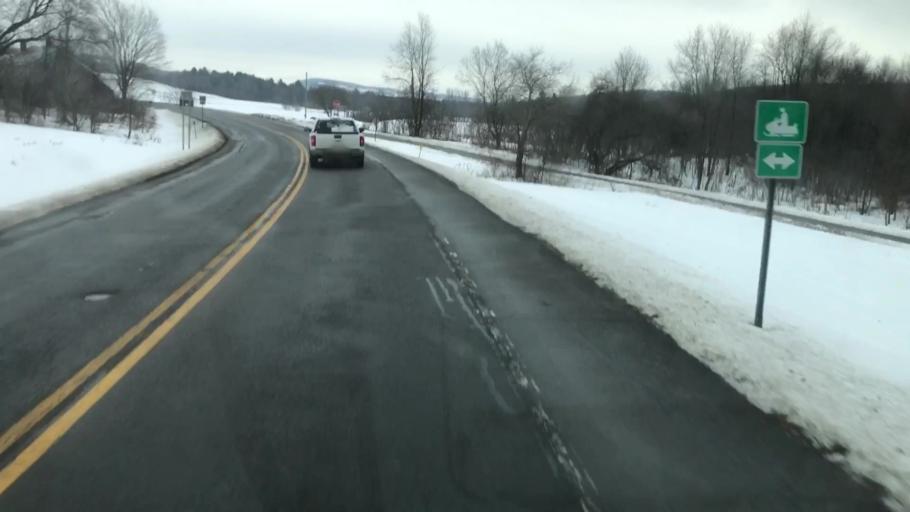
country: US
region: New York
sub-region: Tompkins County
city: Groton
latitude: 42.6822
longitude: -76.3008
